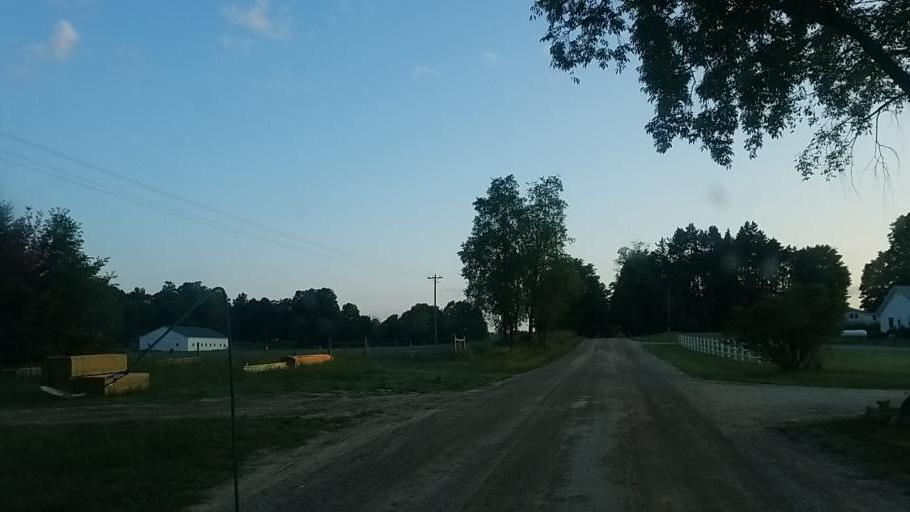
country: US
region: Michigan
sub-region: Osceola County
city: Evart
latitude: 43.9126
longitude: -85.2066
